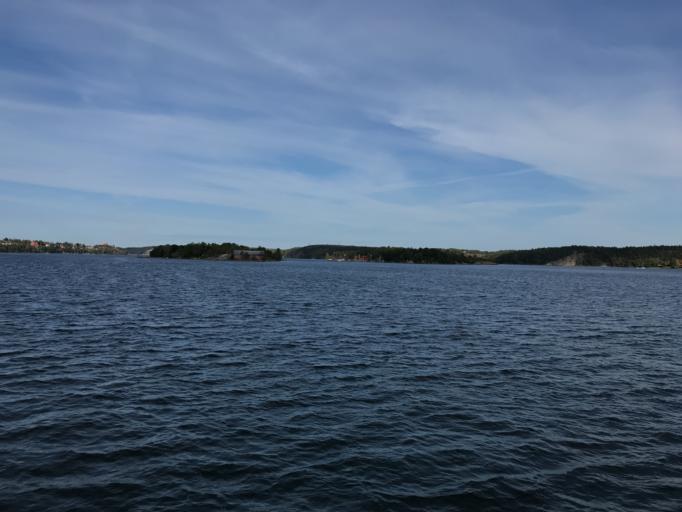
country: SE
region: Stockholm
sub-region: Nacka Kommun
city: Nacka
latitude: 59.3296
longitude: 18.1567
